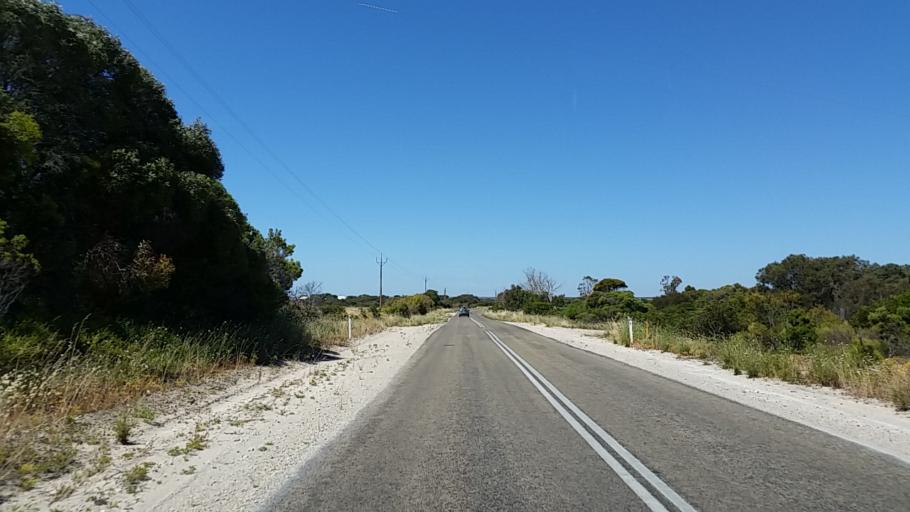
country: AU
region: South Australia
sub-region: Yorke Peninsula
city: Honiton
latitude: -35.2273
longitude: 136.9868
